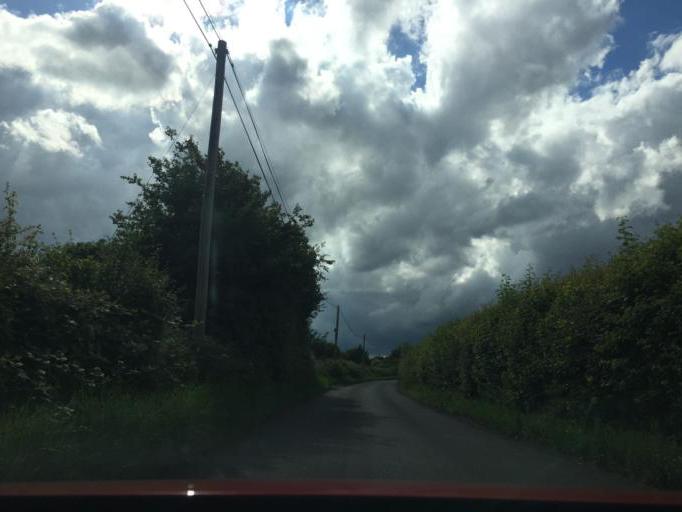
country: GB
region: England
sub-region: Hertfordshire
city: Harpenden
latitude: 51.8534
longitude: -0.3226
